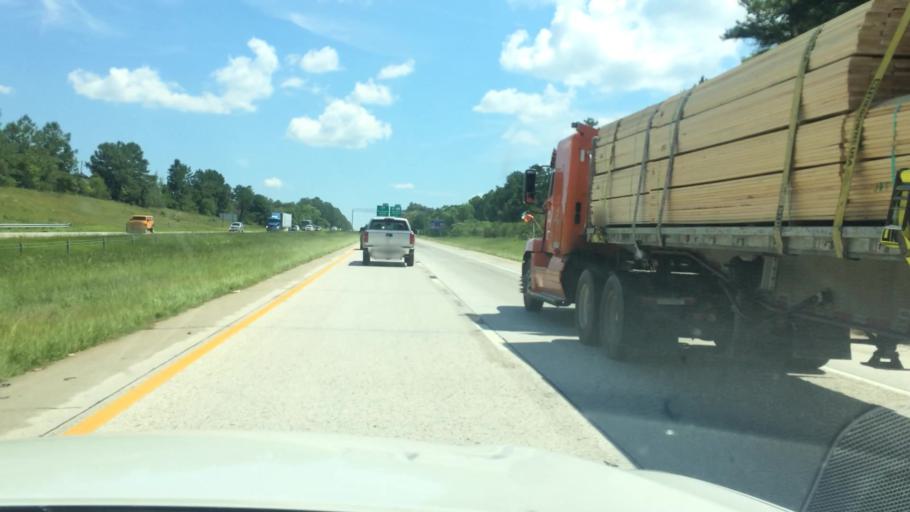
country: US
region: South Carolina
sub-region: Aiken County
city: Belvedere
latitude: 33.5532
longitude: -81.9498
